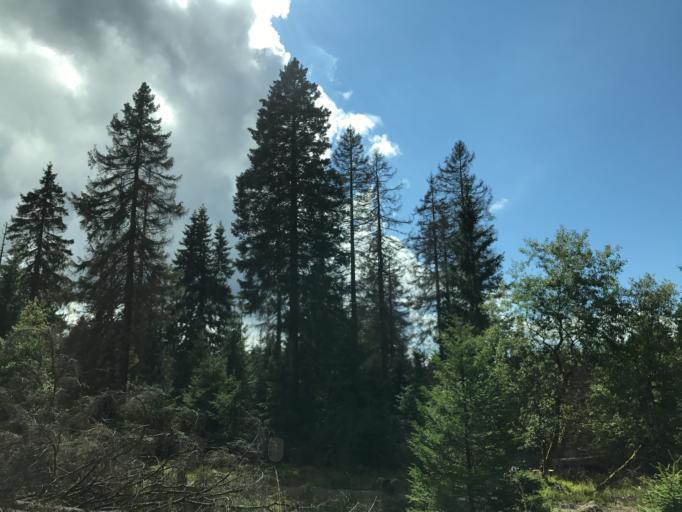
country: DE
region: Lower Saxony
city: Sankt Andreasberg
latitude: 51.7644
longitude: 10.5393
